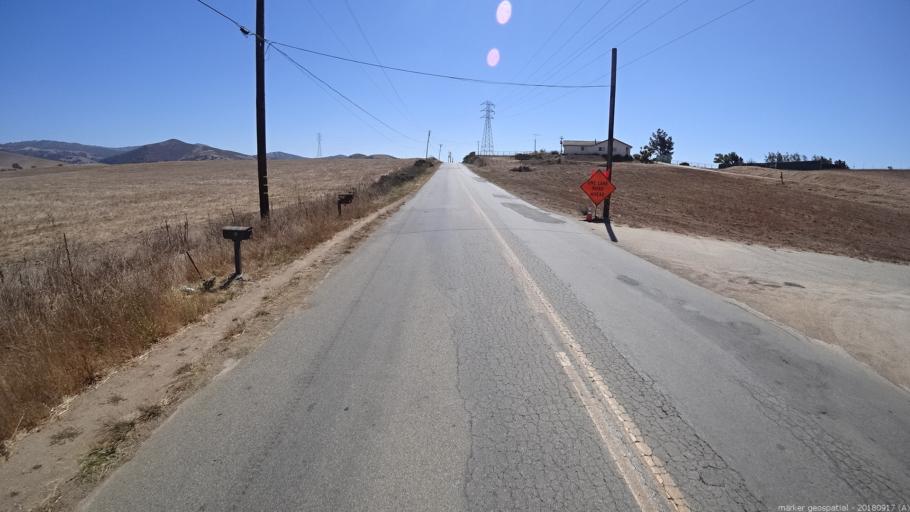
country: US
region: California
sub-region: Monterey County
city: Salinas
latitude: 36.7029
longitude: -121.5782
